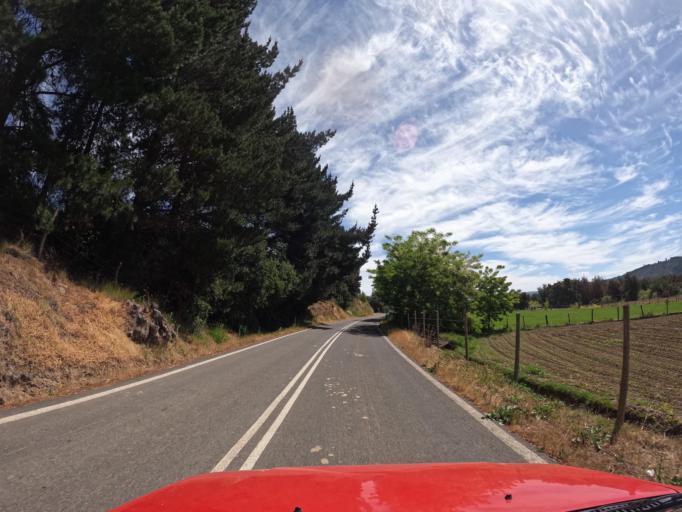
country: CL
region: Maule
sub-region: Provincia de Talca
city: Talca
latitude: -34.9906
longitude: -71.8490
